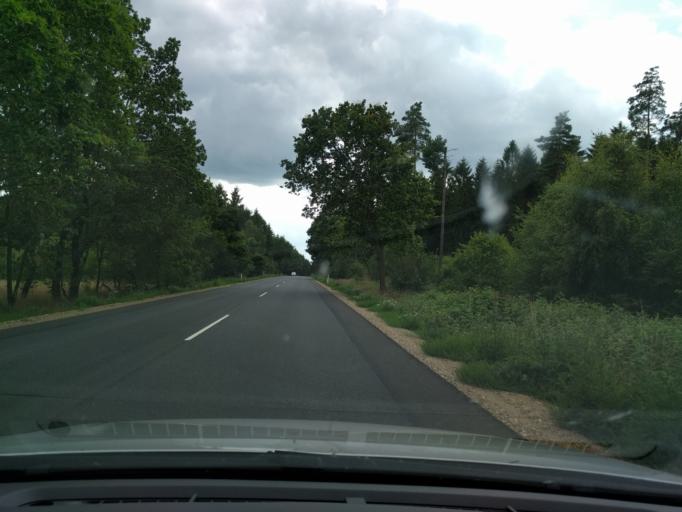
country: DK
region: Central Jutland
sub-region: Silkeborg Kommune
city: Svejbaek
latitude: 56.2033
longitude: 9.7223
